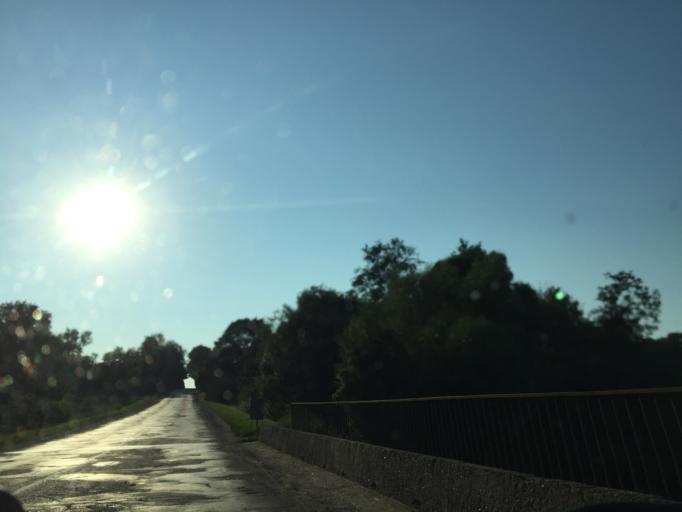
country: LV
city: Tervete
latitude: 56.4337
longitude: 23.5293
